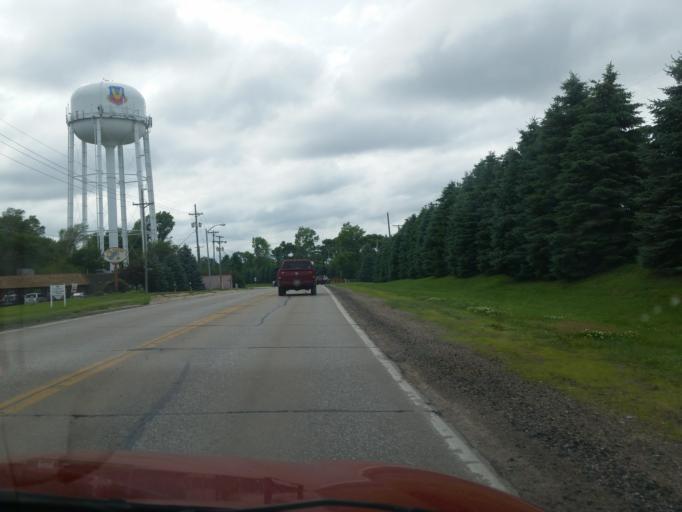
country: US
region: Nebraska
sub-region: Sarpy County
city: Offutt Air Force Base
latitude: 41.1210
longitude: -95.9550
